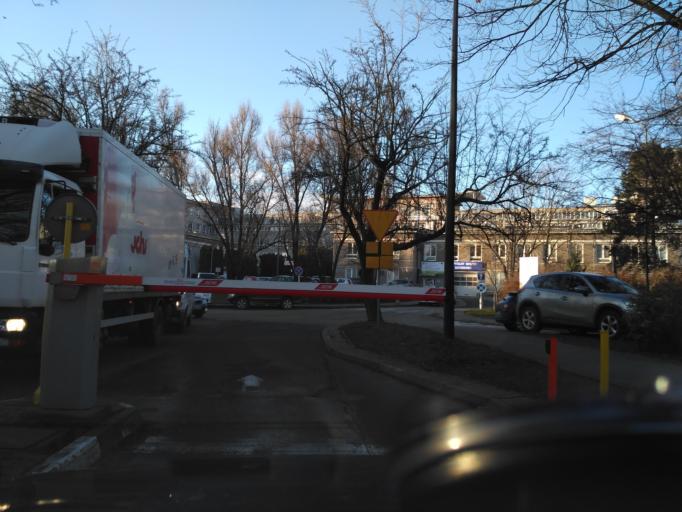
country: PL
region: Lublin Voivodeship
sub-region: Powiat lubelski
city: Lublin
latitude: 51.2595
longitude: 22.5665
